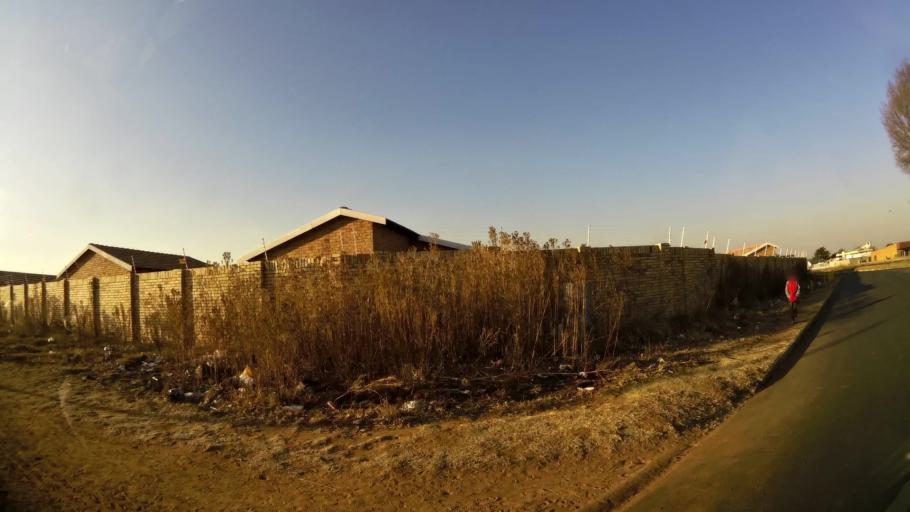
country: ZA
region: Gauteng
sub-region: West Rand District Municipality
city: Randfontein
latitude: -26.2093
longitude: 27.6535
